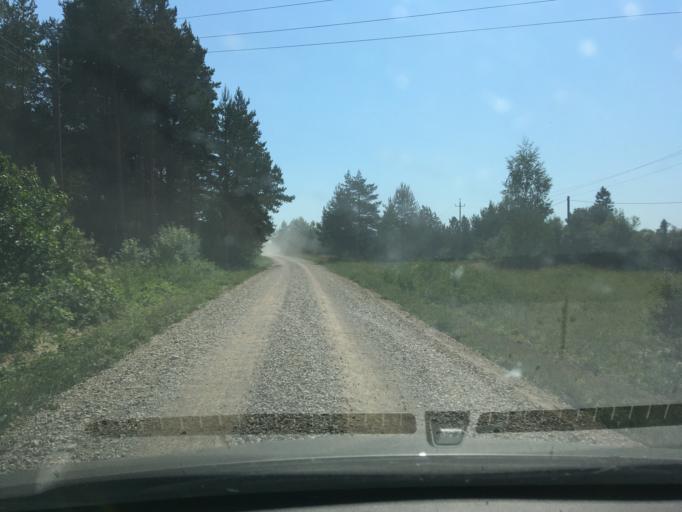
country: EE
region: Laeaene
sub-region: Lihula vald
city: Lihula
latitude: 58.5871
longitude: 23.7140
